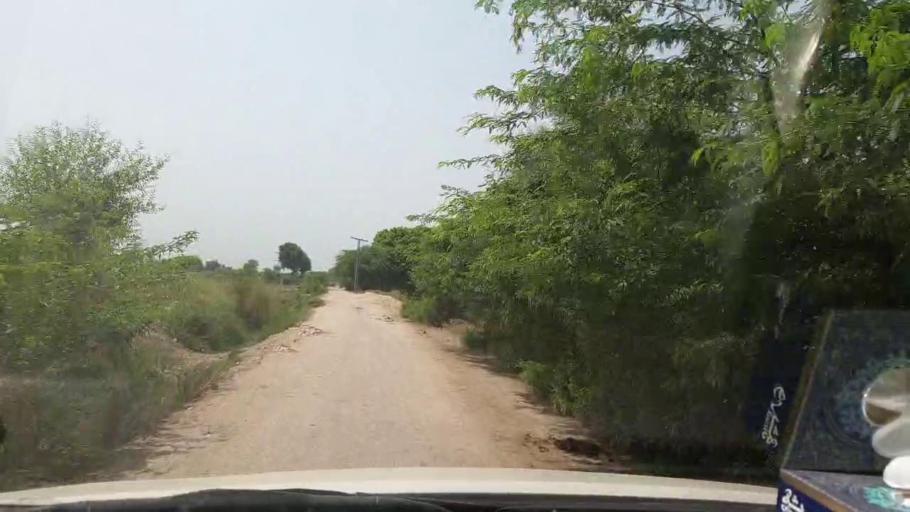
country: PK
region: Sindh
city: Shikarpur
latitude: 27.9926
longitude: 68.7125
